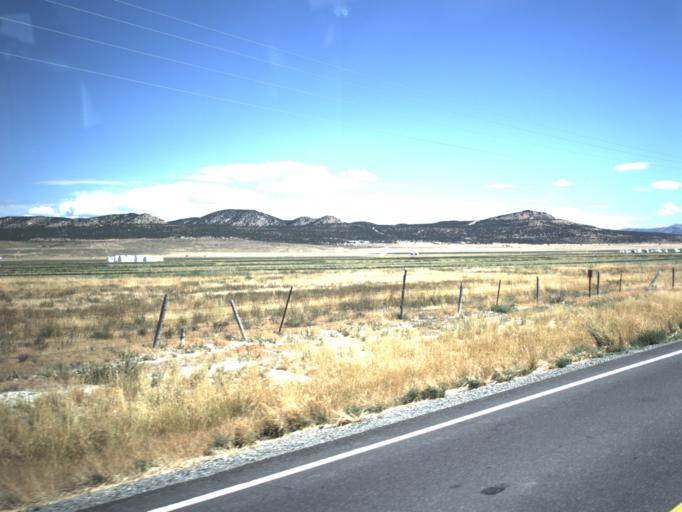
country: US
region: Idaho
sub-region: Oneida County
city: Malad City
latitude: 41.9673
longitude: -112.8320
